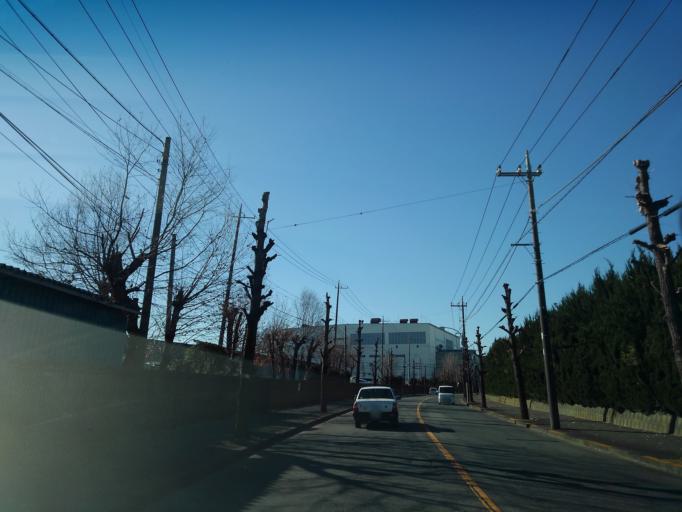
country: JP
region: Tokyo
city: Fussa
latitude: 35.7764
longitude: 139.3200
